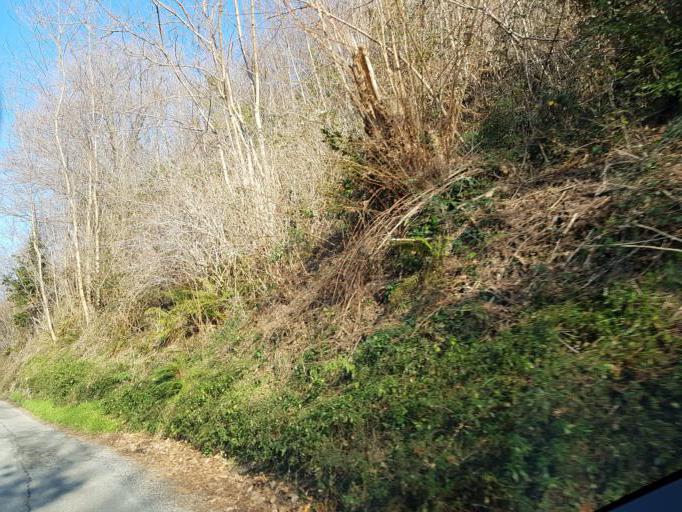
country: IT
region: Liguria
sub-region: Provincia di Genova
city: Santa Marta
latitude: 44.4967
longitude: 8.8828
